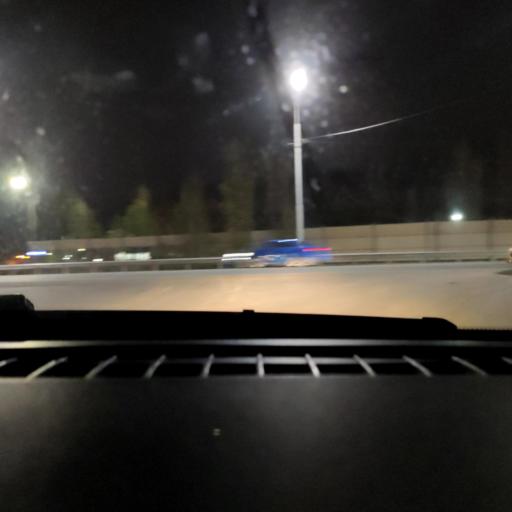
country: RU
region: Voronezj
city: Somovo
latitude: 51.6770
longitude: 39.3201
